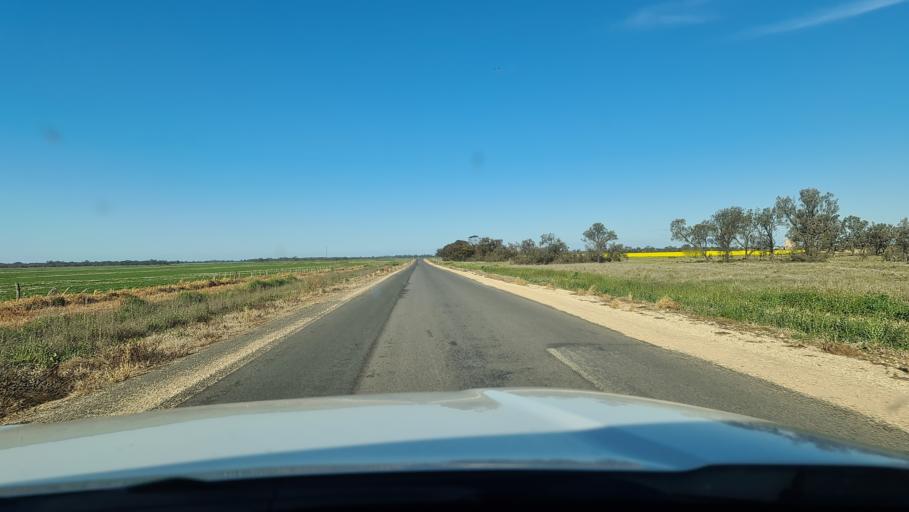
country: AU
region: Victoria
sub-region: Horsham
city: Horsham
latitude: -36.4492
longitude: 142.5611
